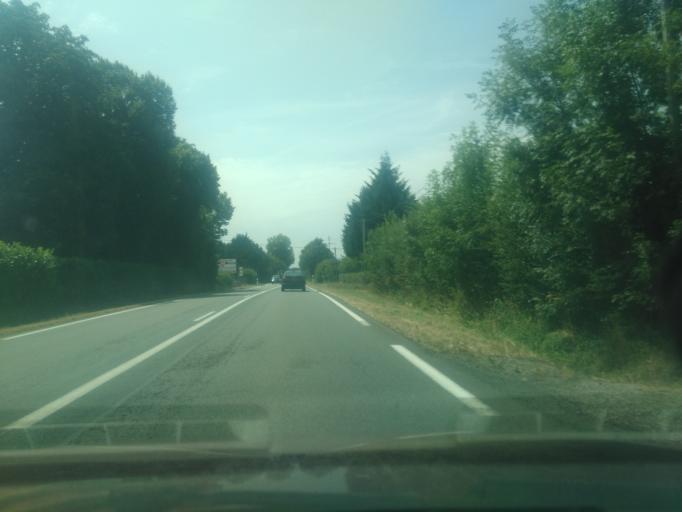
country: FR
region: Poitou-Charentes
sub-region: Departement des Deux-Sevres
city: Thenezay
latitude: 46.6557
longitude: -0.0674
